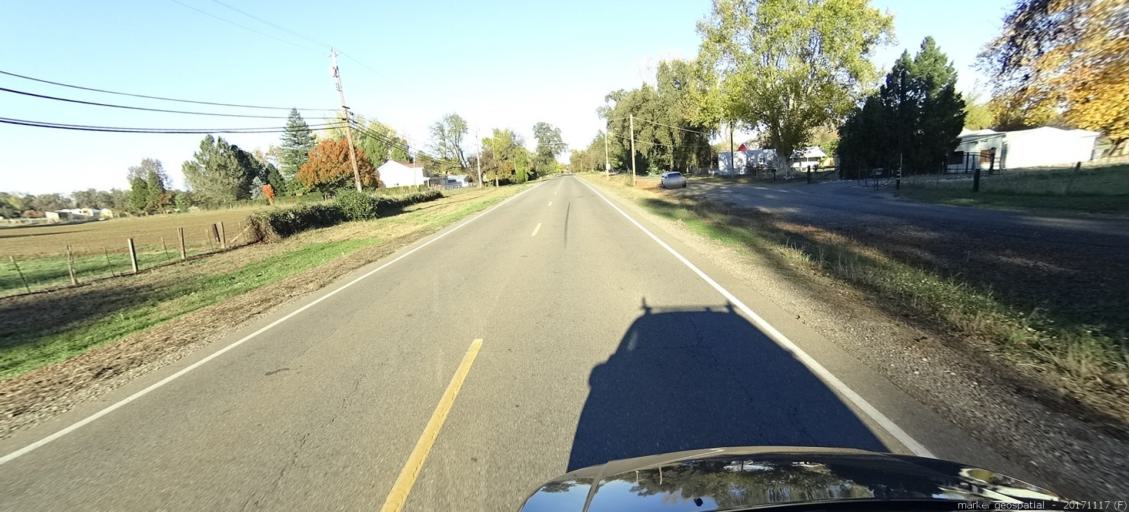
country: US
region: California
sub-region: Shasta County
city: Anderson
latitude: 40.4546
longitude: -122.2493
